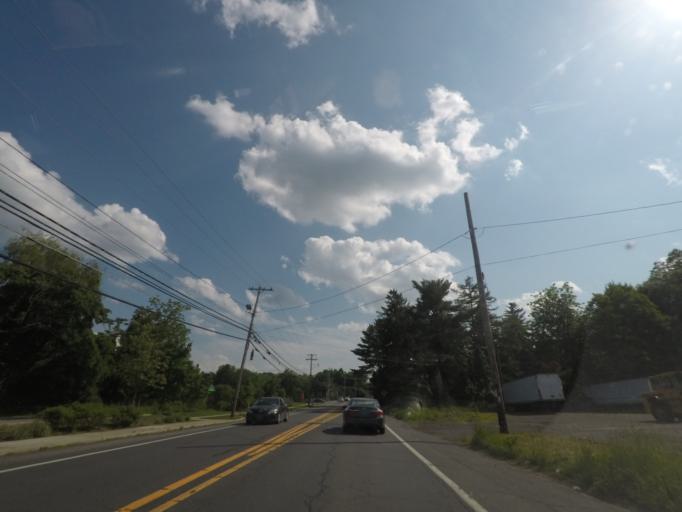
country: US
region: New York
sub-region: Orange County
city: Balmville
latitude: 41.5497
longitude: -74.0059
